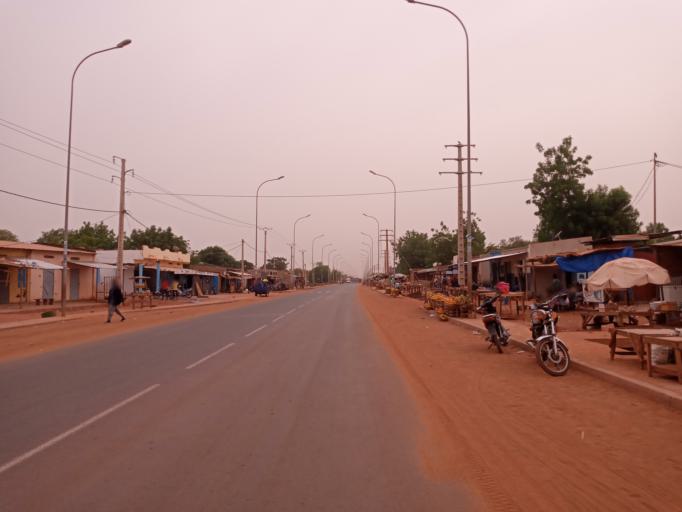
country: ML
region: Koulikoro
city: Koulikoro
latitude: 12.8444
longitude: -7.5829
